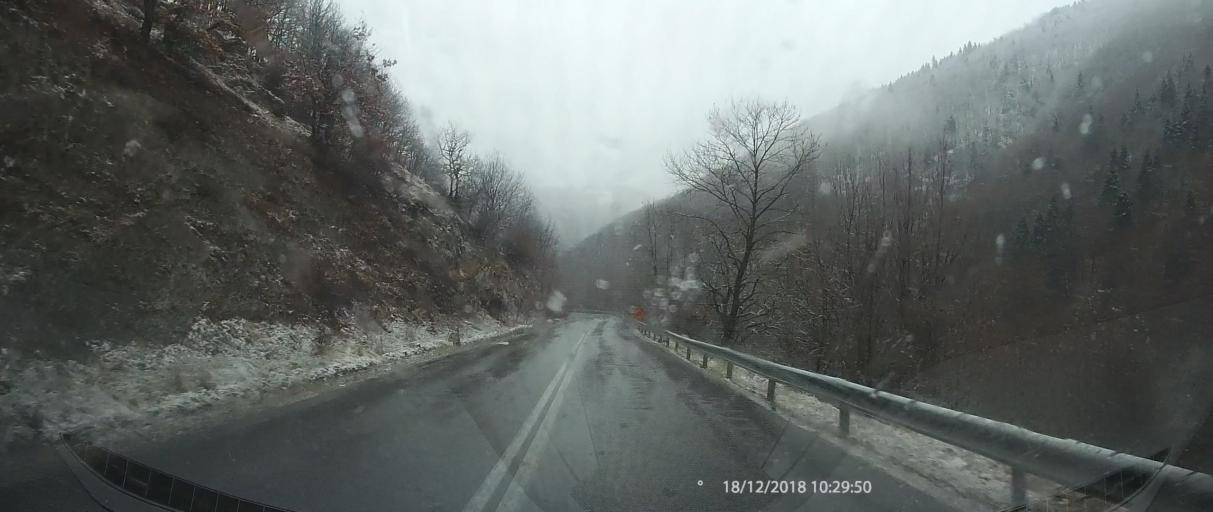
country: GR
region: Central Macedonia
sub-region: Nomos Pierias
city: Kato Milia
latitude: 40.1849
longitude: 22.2742
